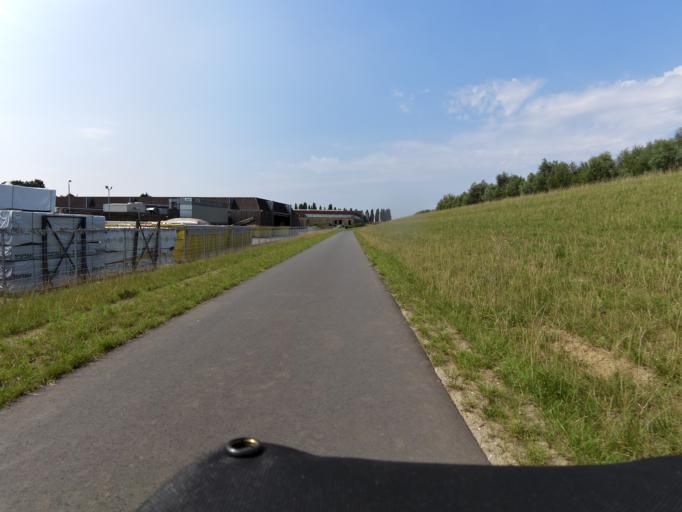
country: NL
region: South Holland
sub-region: Gemeente Binnenmaas
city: Heinenoord
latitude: 51.8287
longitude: 4.4632
